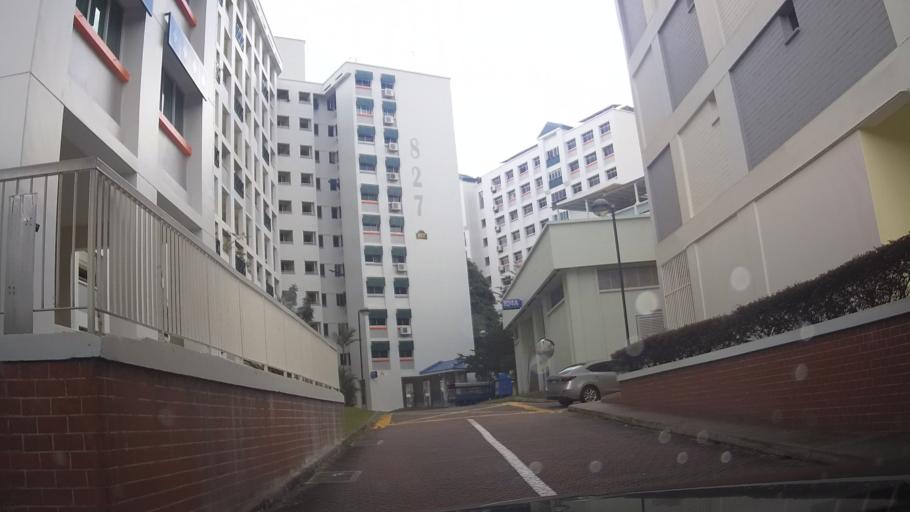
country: MY
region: Johor
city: Johor Bahru
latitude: 1.4400
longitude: 103.7890
